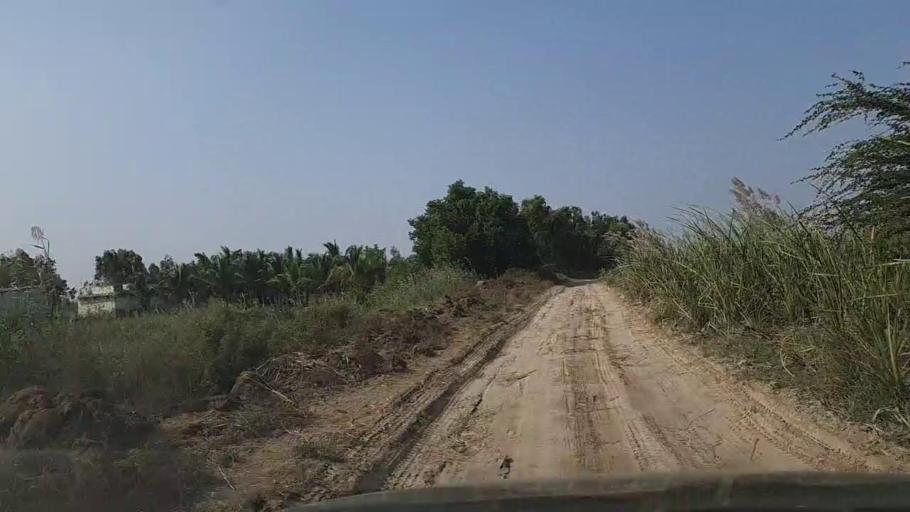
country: PK
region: Sindh
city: Gharo
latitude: 24.7222
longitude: 67.6808
